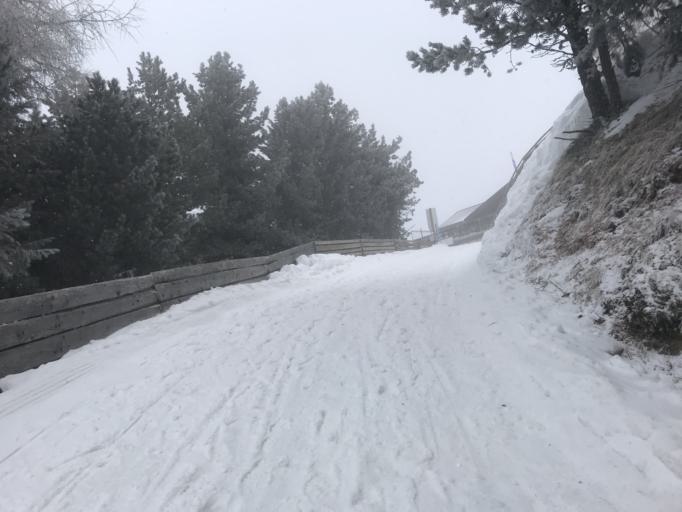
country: IT
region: Trentino-Alto Adige
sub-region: Bolzano
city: San Pietro
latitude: 46.6848
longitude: 11.7098
